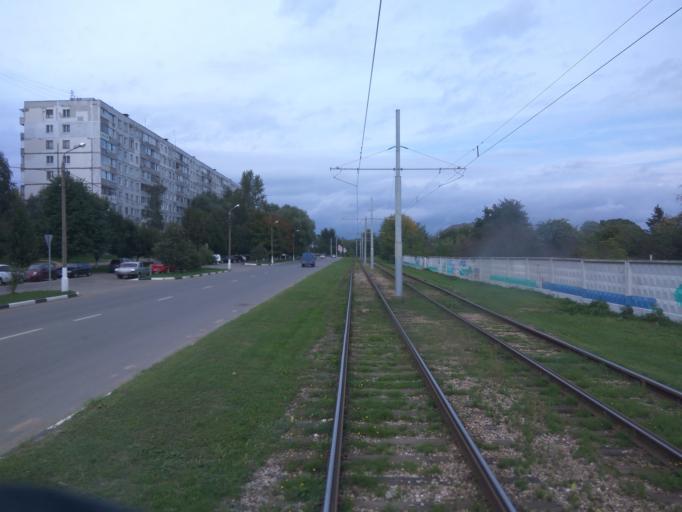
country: RU
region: Moskovskaya
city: Kolomna
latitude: 55.0590
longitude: 38.7548
